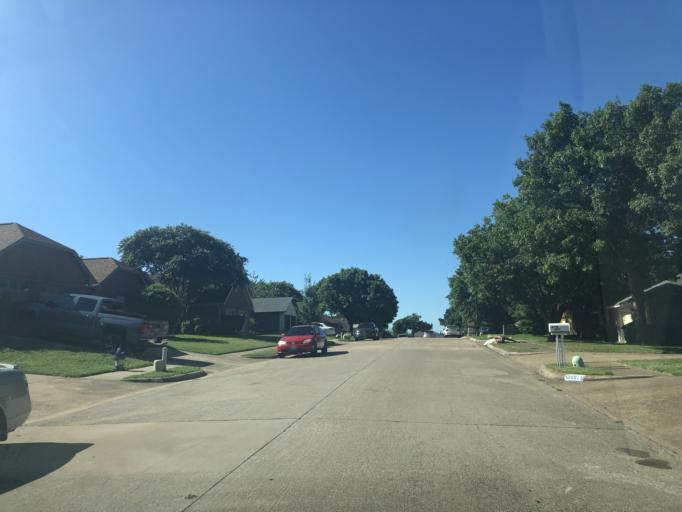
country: US
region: Texas
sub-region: Dallas County
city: Duncanville
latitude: 32.6643
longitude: -96.9338
